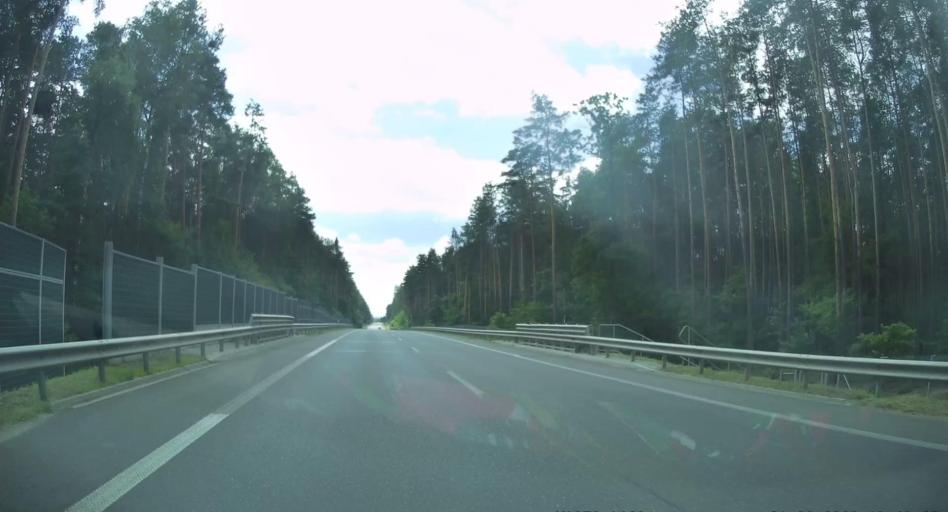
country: PL
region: Subcarpathian Voivodeship
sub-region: Powiat mielecki
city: Mielec
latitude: 50.2723
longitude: 21.4961
